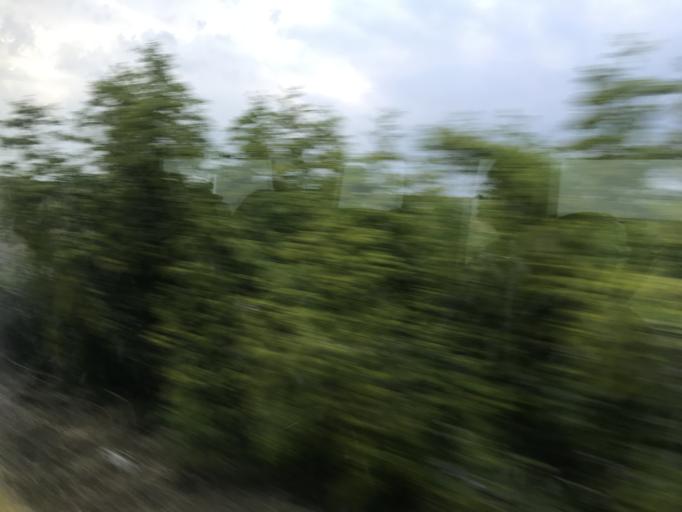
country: GR
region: East Macedonia and Thrace
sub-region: Nomos Rodopis
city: Arisvi
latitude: 41.0773
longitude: 25.5809
